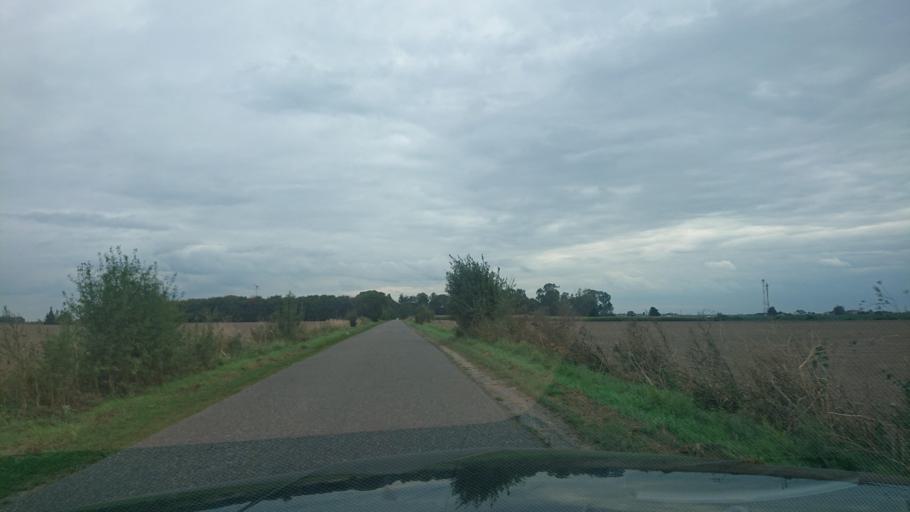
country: PL
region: Greater Poland Voivodeship
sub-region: Powiat gnieznienski
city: Niechanowo
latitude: 52.4615
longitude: 17.6203
